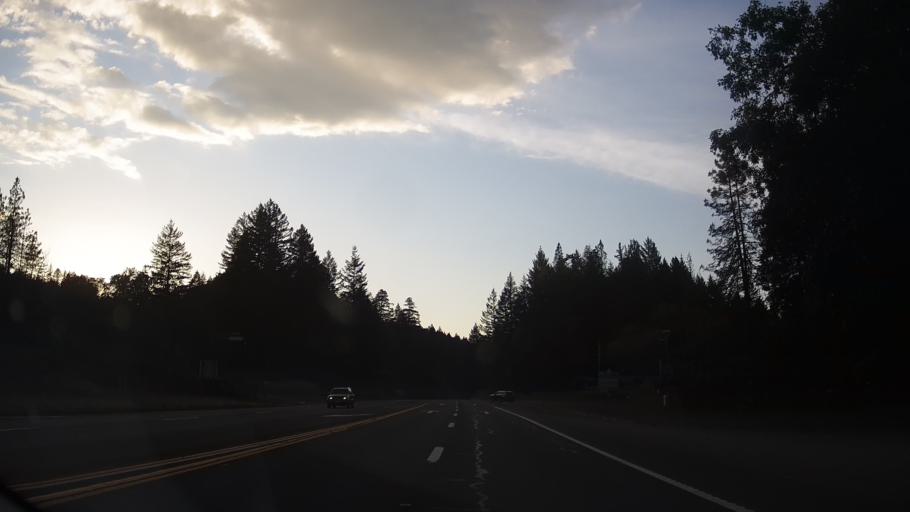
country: US
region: California
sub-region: Mendocino County
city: Willits
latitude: 39.3446
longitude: -123.3184
